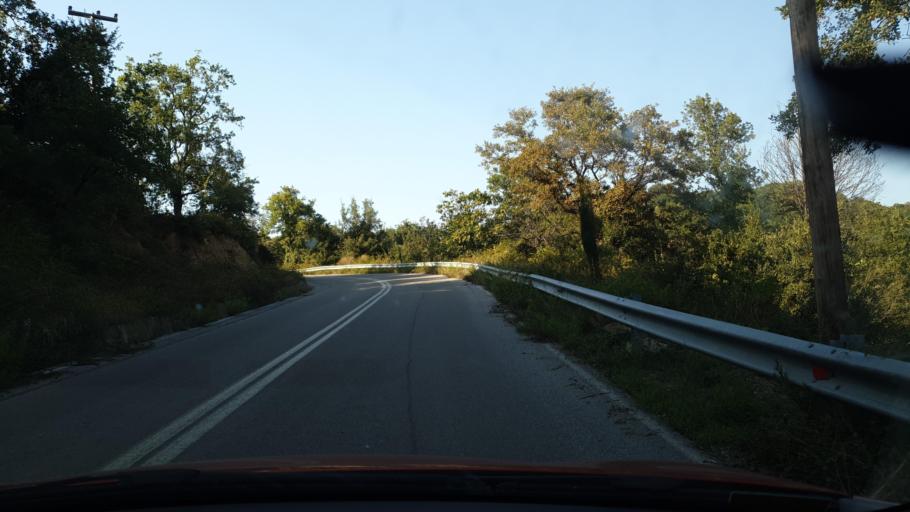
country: GR
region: Central Greece
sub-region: Nomos Evvoias
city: Kymi
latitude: 38.6450
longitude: 23.9392
